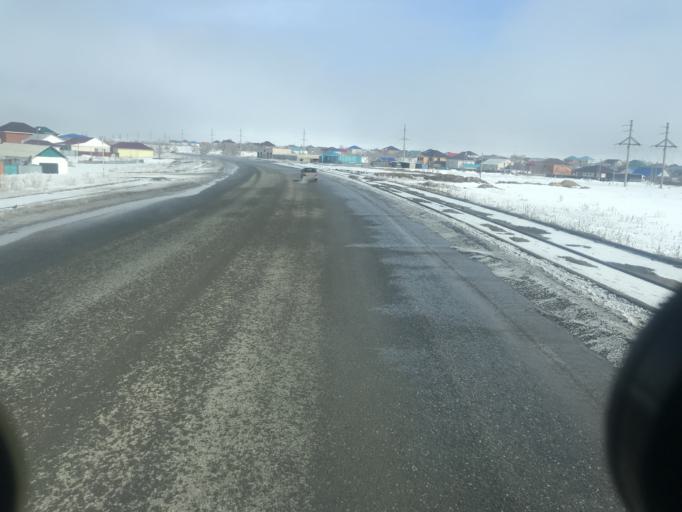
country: KZ
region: Aqtoebe
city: Aqtobe
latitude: 50.2789
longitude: 57.2793
